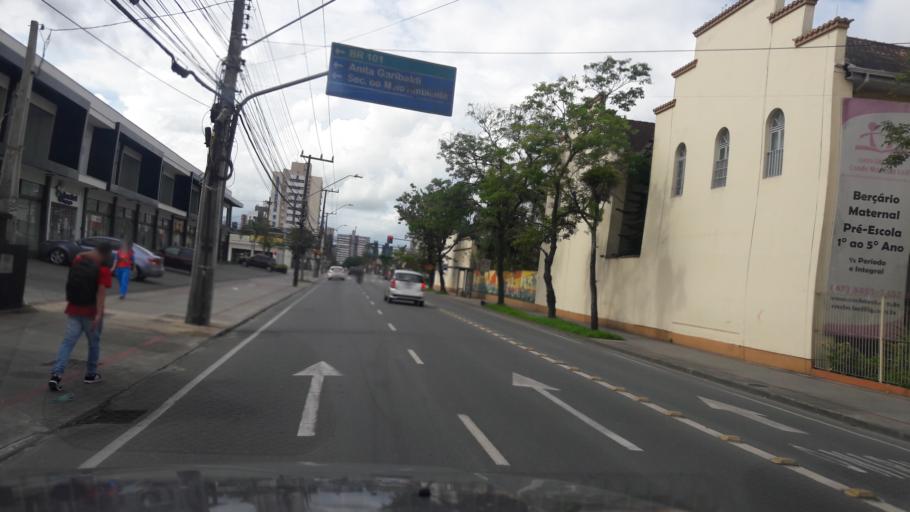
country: BR
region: Santa Catarina
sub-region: Joinville
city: Joinville
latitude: -26.3156
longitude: -48.8427
